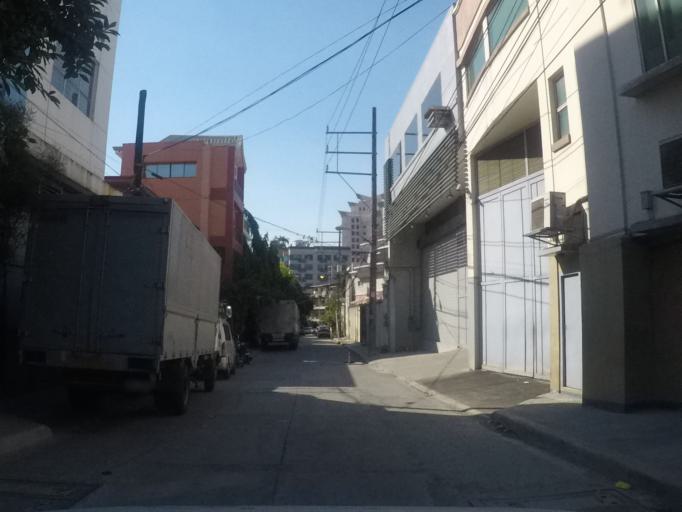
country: PH
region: Metro Manila
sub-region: San Juan
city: San Juan
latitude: 14.6079
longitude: 121.0316
